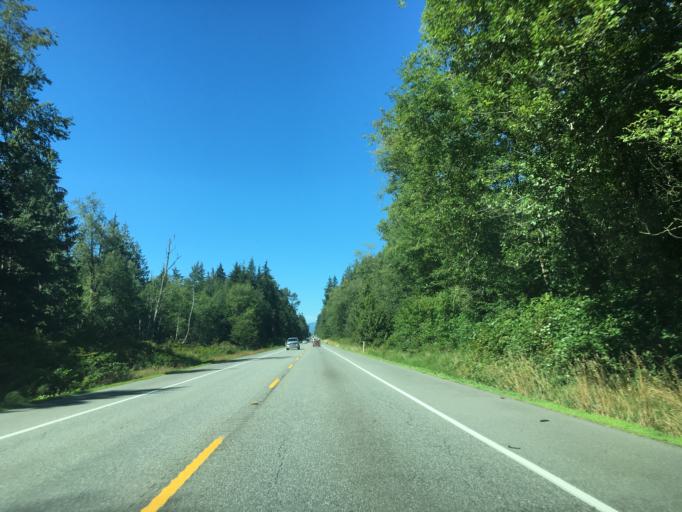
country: US
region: Washington
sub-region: Snohomish County
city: Sisco Heights
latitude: 48.1012
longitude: -122.1121
